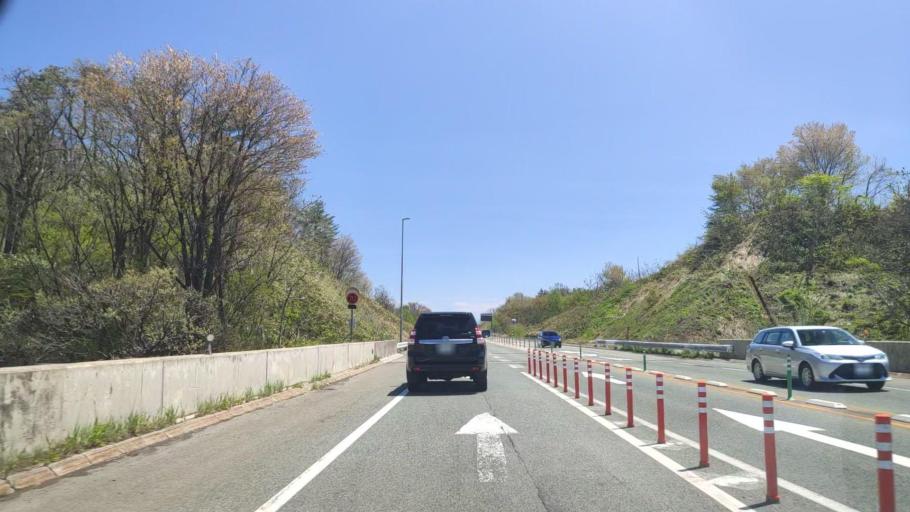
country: JP
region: Yamagata
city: Shinjo
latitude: 38.7369
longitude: 140.3003
